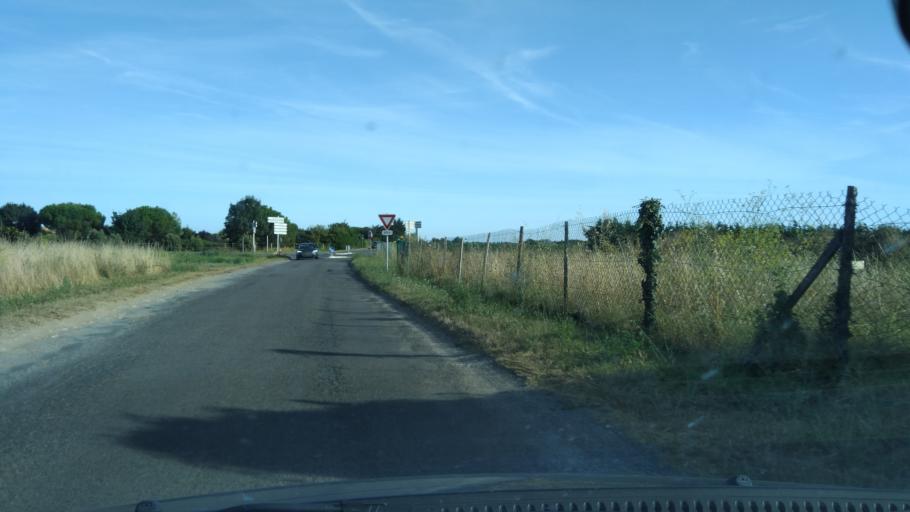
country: FR
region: Poitou-Charentes
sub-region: Departement de la Charente-Maritime
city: Dolus-d'Oleron
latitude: 45.9410
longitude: -1.3399
